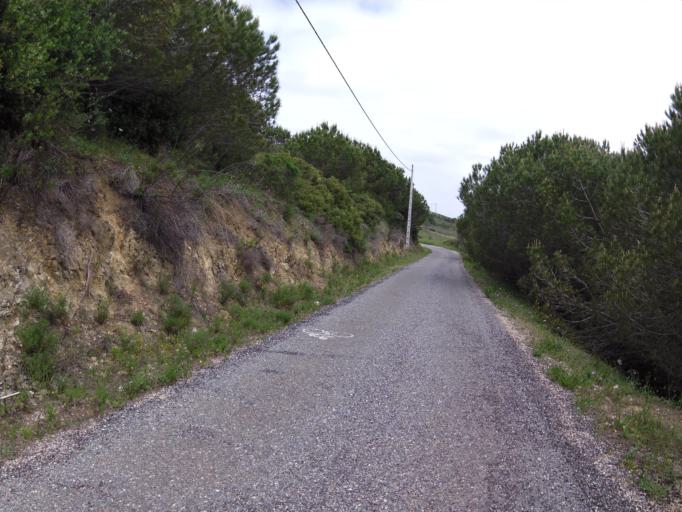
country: PT
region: Faro
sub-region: Vila do Bispo
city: Vila do Bispo
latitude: 37.0745
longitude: -8.8750
